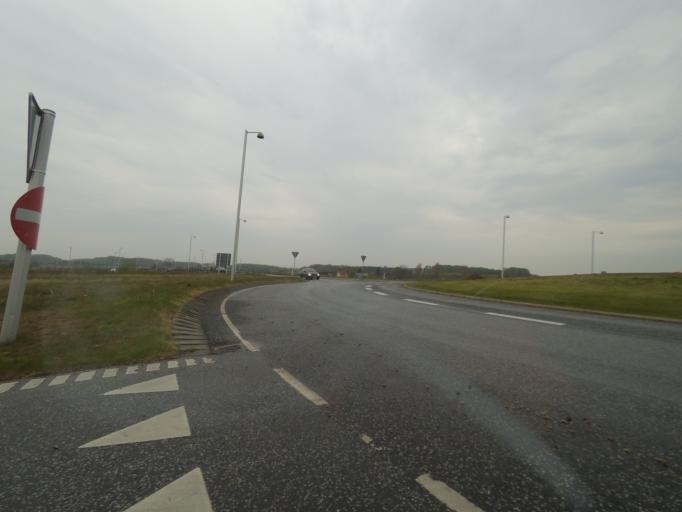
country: DK
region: South Denmark
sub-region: Faaborg-Midtfyn Kommune
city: Ringe
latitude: 55.1899
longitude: 10.5278
